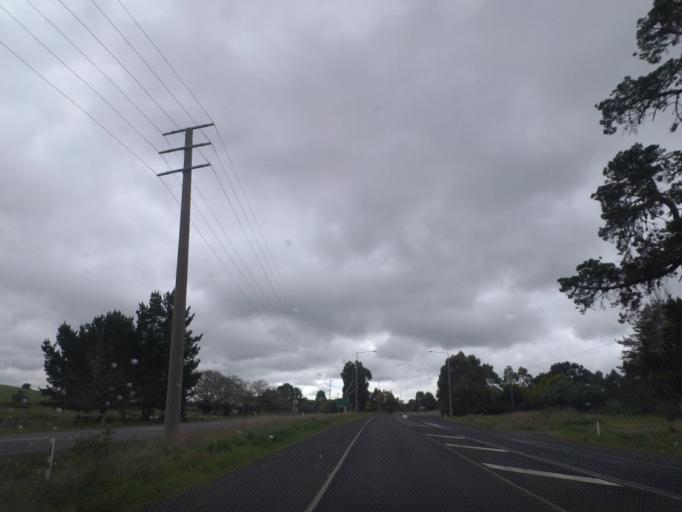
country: AU
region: Victoria
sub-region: Hume
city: Sunbury
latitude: -37.3242
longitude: 144.5237
